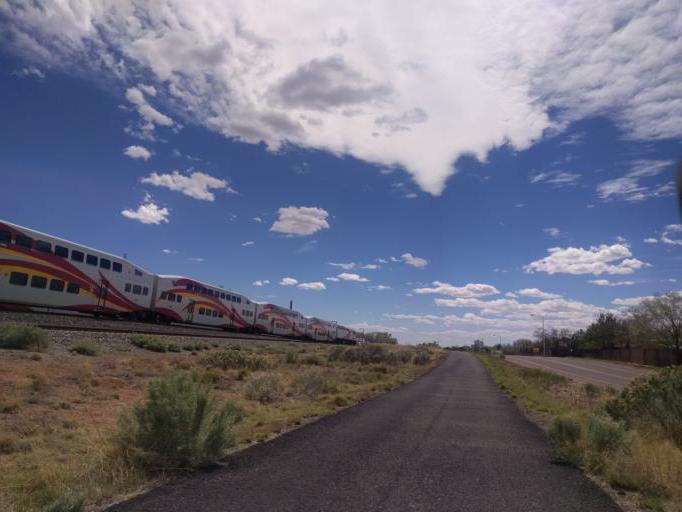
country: US
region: New Mexico
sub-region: Santa Fe County
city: Santa Fe
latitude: 35.6433
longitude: -105.9579
